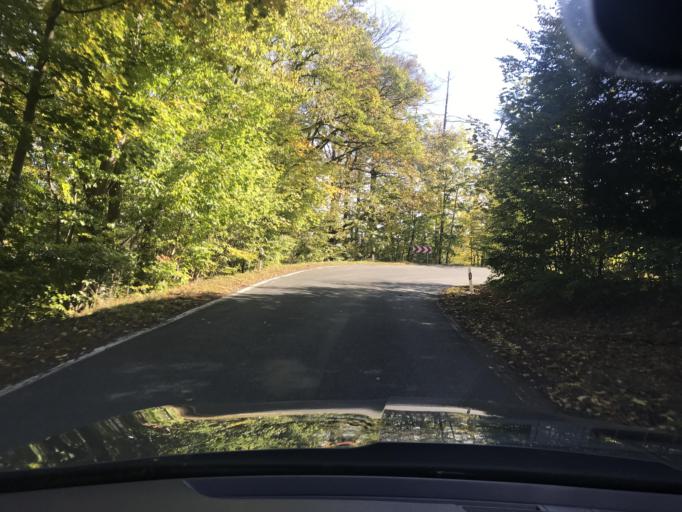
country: DE
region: Saxony-Anhalt
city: Timmenrode
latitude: 51.7380
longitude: 10.9975
